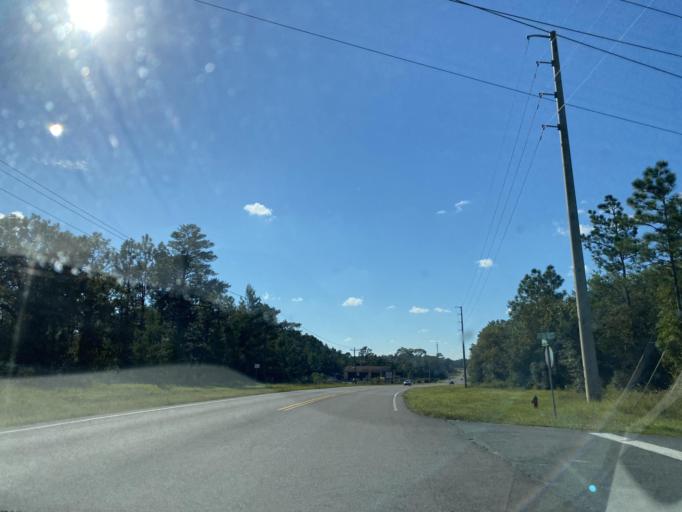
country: US
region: Florida
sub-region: Citrus County
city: Hernando
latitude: 29.0521
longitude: -82.2700
